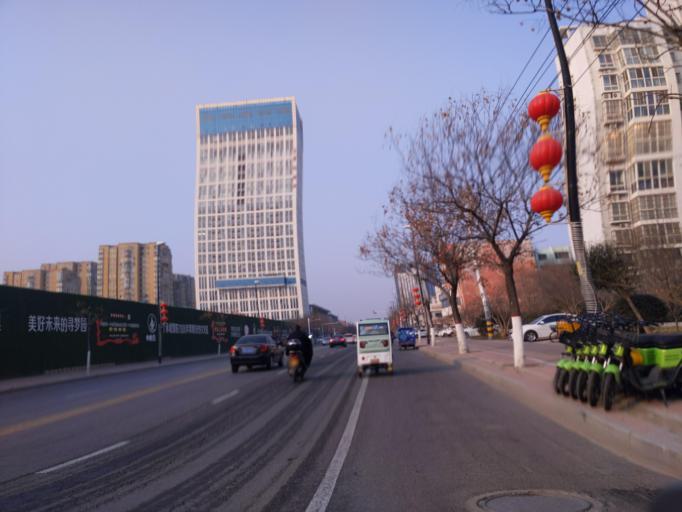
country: CN
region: Henan Sheng
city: Zhongyuanlu
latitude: 35.7658
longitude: 115.0576
